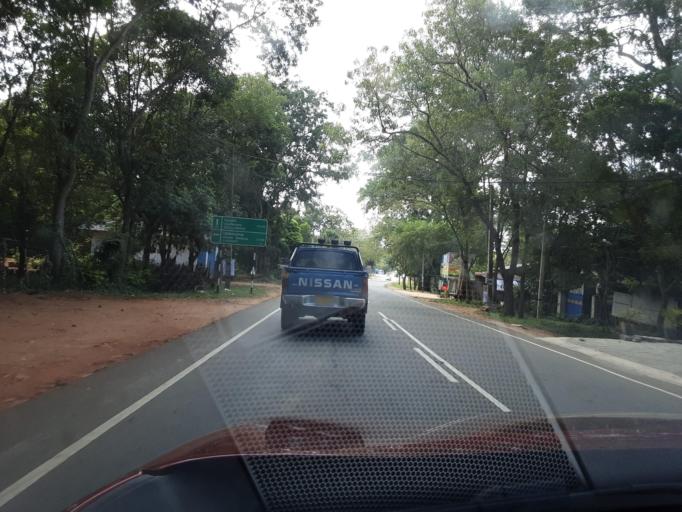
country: LK
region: Uva
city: Haputale
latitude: 6.3594
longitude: 81.1829
